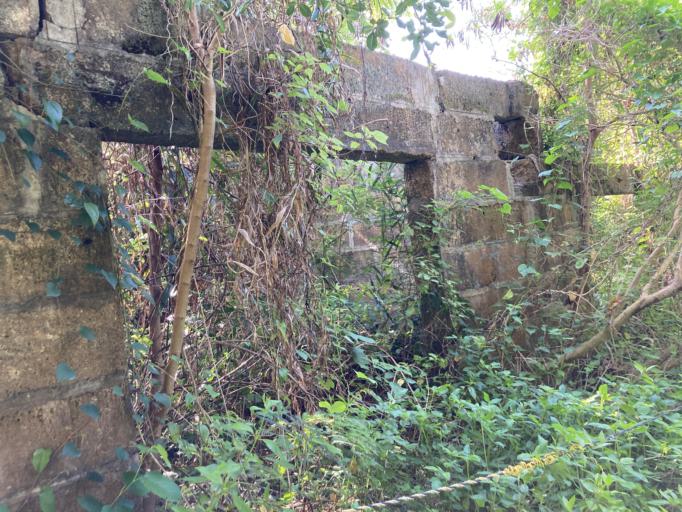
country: JP
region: Okinawa
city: Itoman
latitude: 26.1186
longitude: 127.7469
